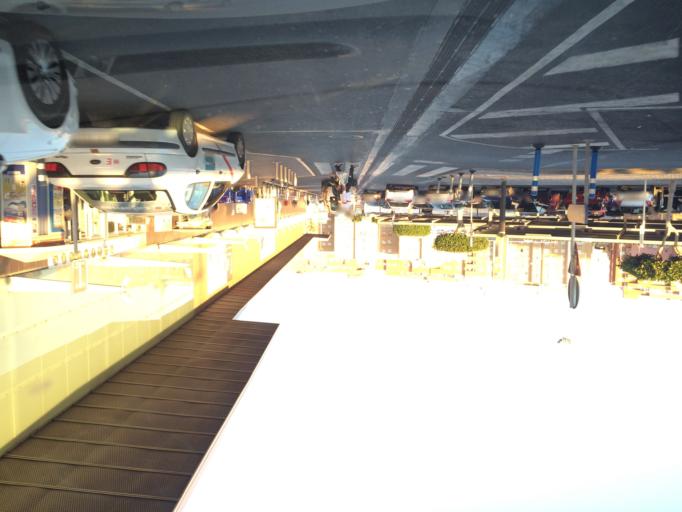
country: ES
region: Andalusia
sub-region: Provincia de Almeria
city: Almeria
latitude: 36.8414
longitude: -2.4446
